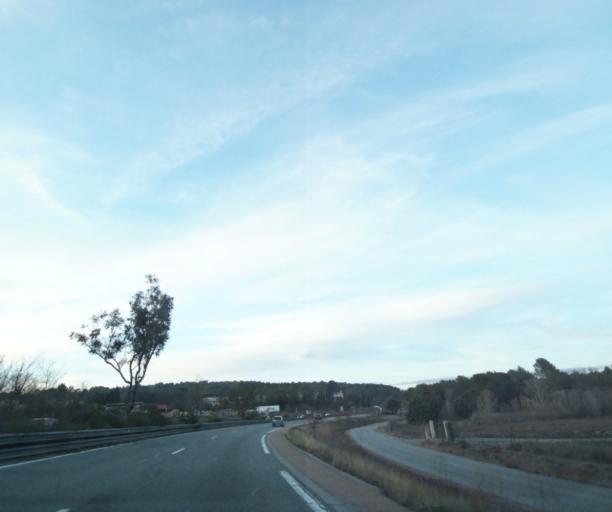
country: FR
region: Provence-Alpes-Cote d'Azur
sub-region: Departement du Var
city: La Motte
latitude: 43.4816
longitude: 6.5105
